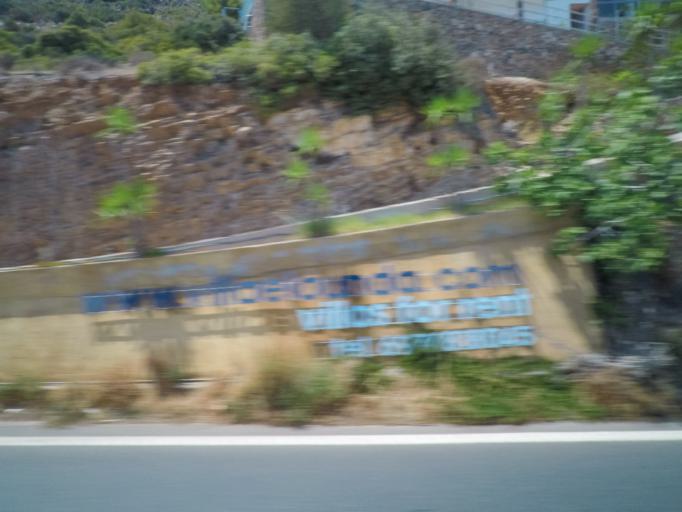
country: GR
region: Crete
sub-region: Nomos Lasithiou
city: Skhisma
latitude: 35.2355
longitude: 25.7282
